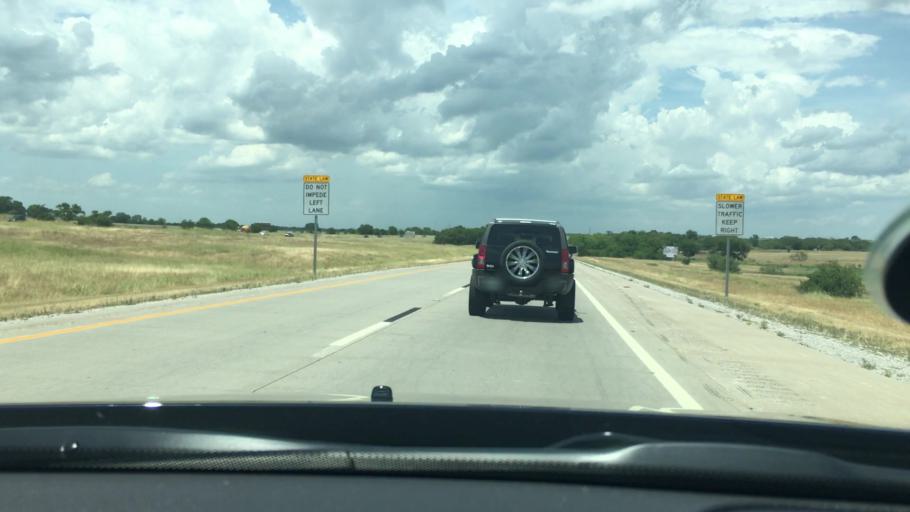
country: US
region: Oklahoma
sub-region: Carter County
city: Ardmore
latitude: 34.0875
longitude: -97.1500
